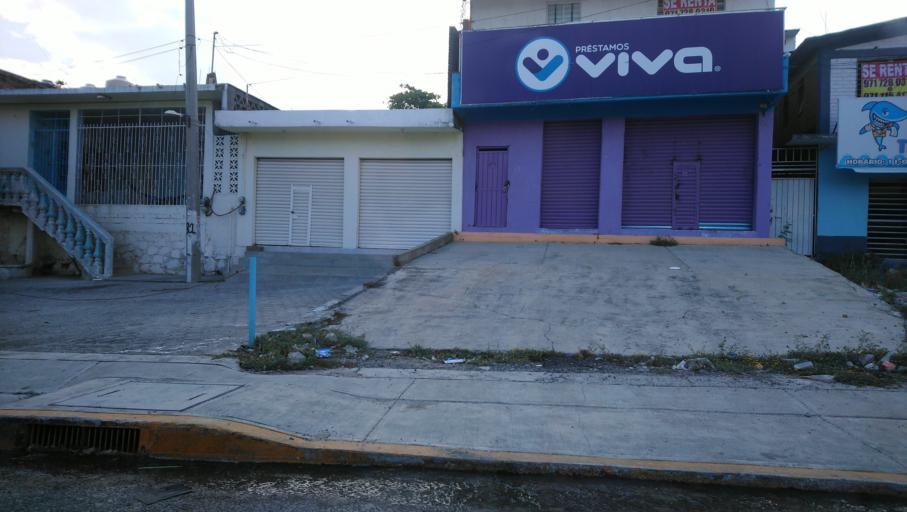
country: MX
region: Oaxaca
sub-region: Salina Cruz
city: Salina Cruz
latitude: 16.1981
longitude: -95.2017
